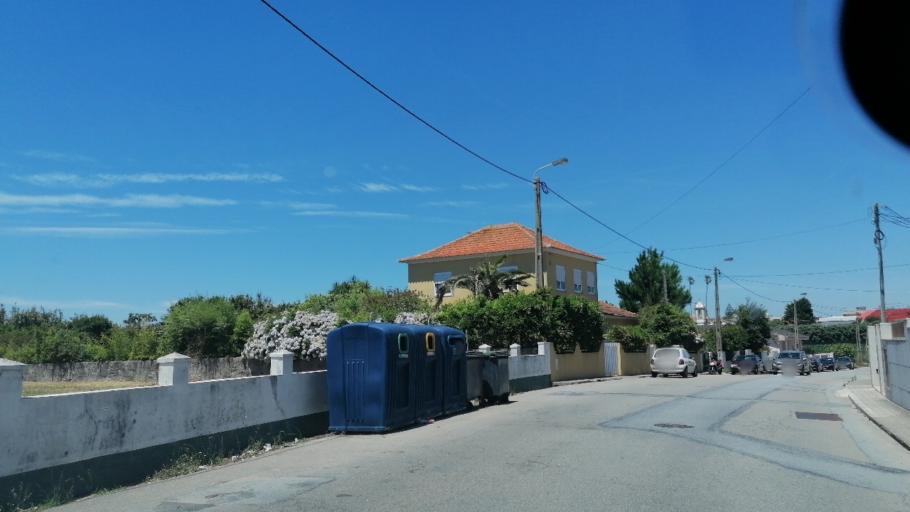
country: PT
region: Porto
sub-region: Matosinhos
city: Lavra
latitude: 41.2564
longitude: -8.7188
